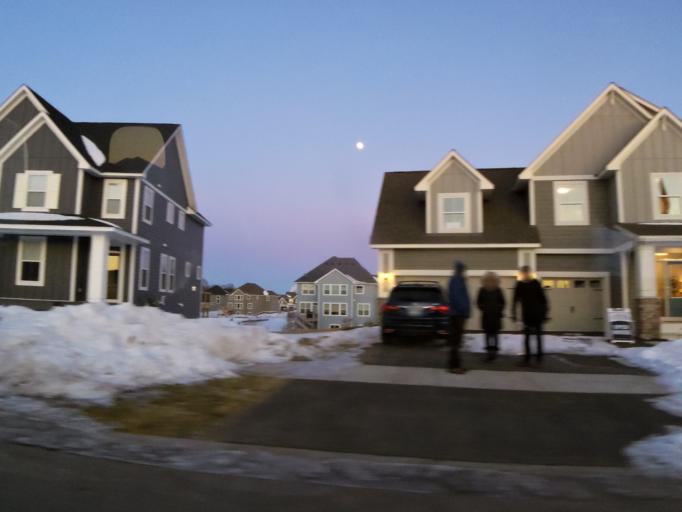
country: US
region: Minnesota
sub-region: Washington County
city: Lake Elmo
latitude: 45.0091
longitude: -92.8788
